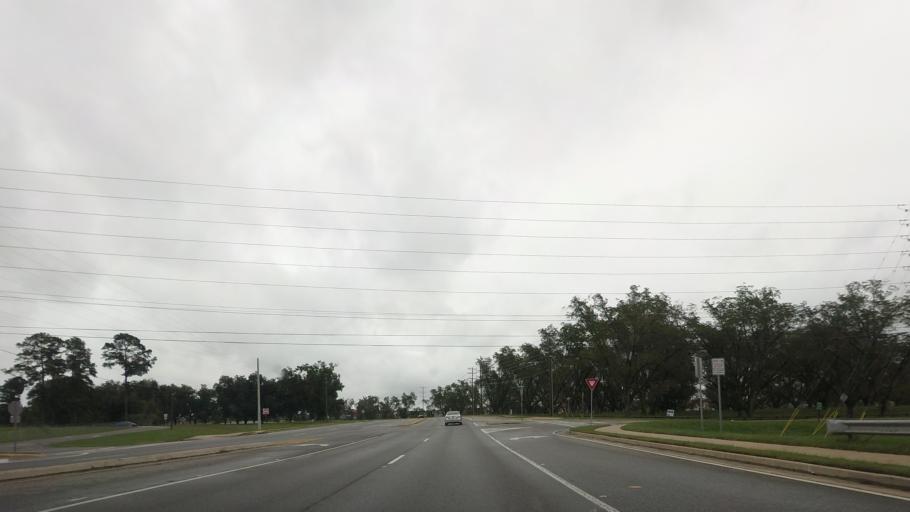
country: US
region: Georgia
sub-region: Houston County
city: Perry
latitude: 32.4990
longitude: -83.6658
